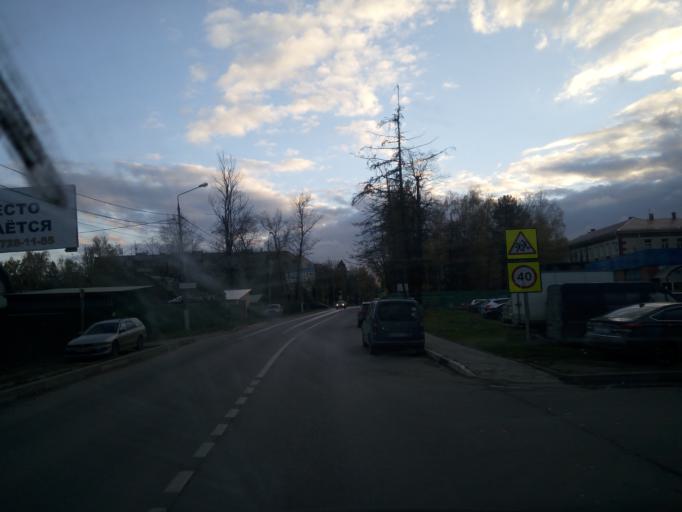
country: RU
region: Moskovskaya
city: Skhodnya
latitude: 55.9576
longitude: 37.3055
